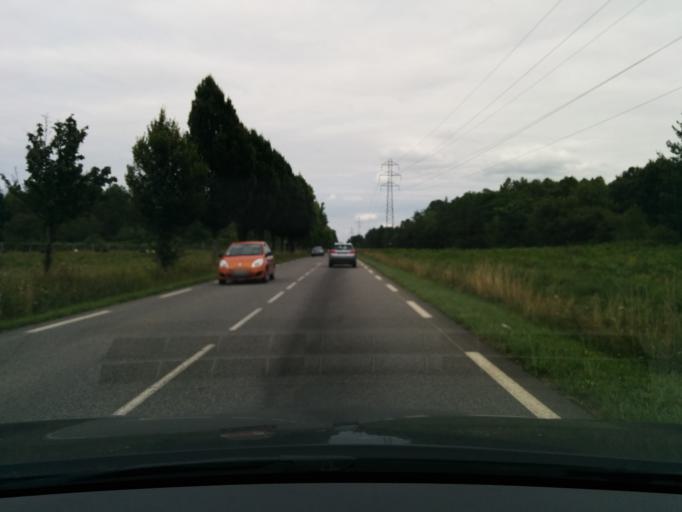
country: FR
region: Midi-Pyrenees
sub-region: Departement des Hautes-Pyrenees
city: La Barthe-de-Neste
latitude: 43.0831
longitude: 0.3637
